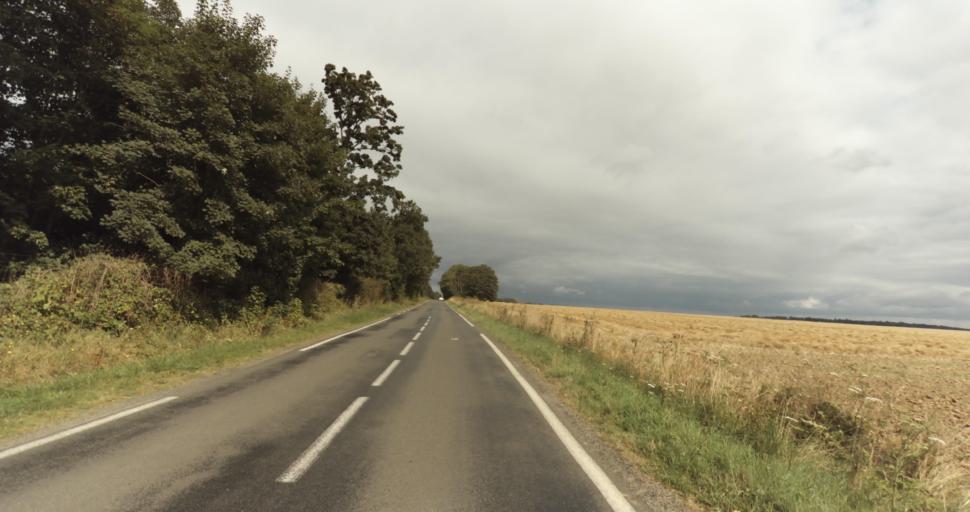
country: FR
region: Haute-Normandie
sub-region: Departement de l'Eure
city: Gravigny
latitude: 49.0160
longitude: 1.2451
